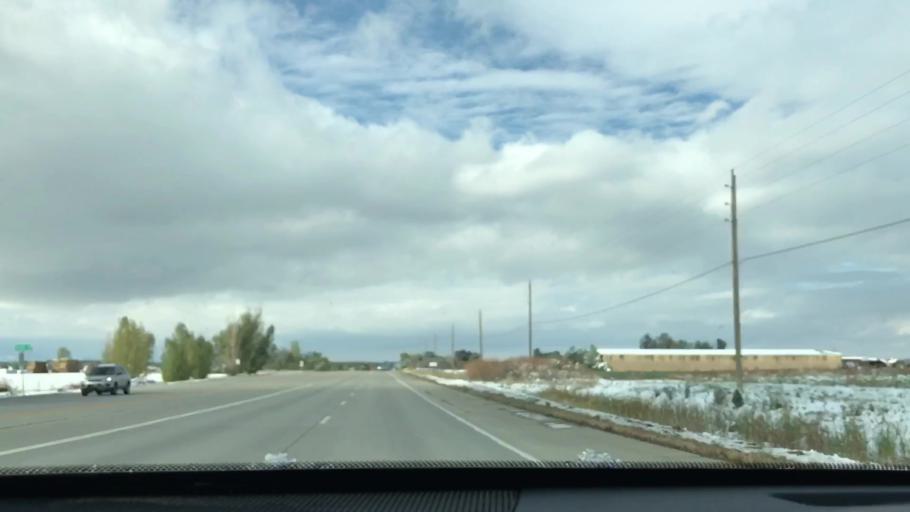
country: US
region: Colorado
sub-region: Boulder County
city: Longmont
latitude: 40.1228
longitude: -105.1025
